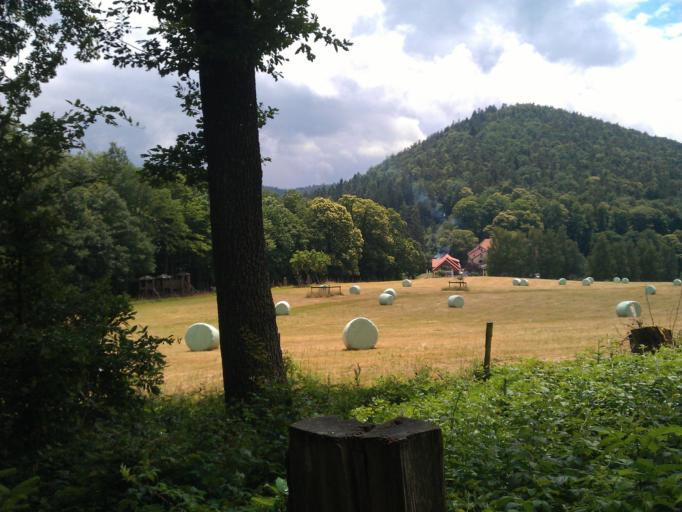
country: DE
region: Rheinland-Pfalz
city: Nothweiler
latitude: 49.0495
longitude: 7.7878
